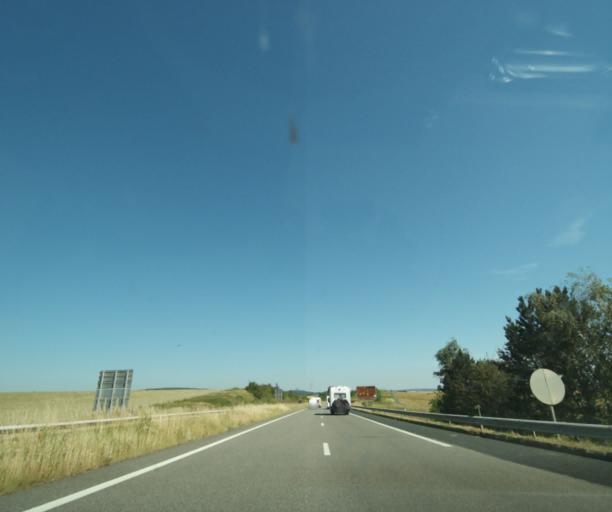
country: FR
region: Lorraine
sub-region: Departement des Vosges
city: Chatenois
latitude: 48.2748
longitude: 5.8576
